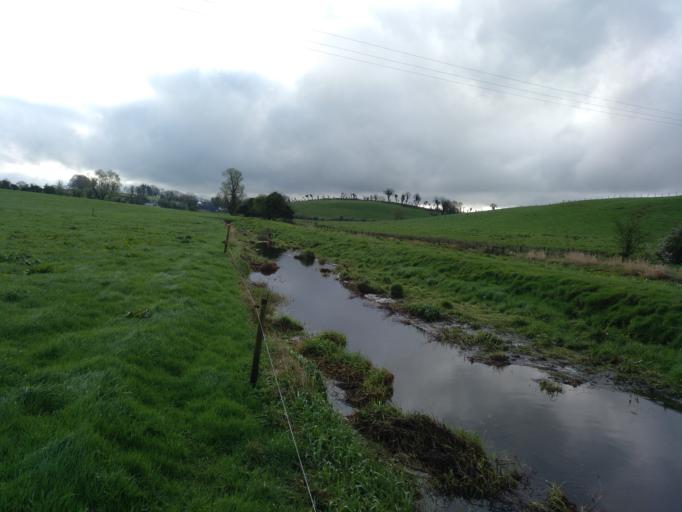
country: IE
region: Ulster
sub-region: County Monaghan
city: Clones
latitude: 54.1736
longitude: -7.2214
